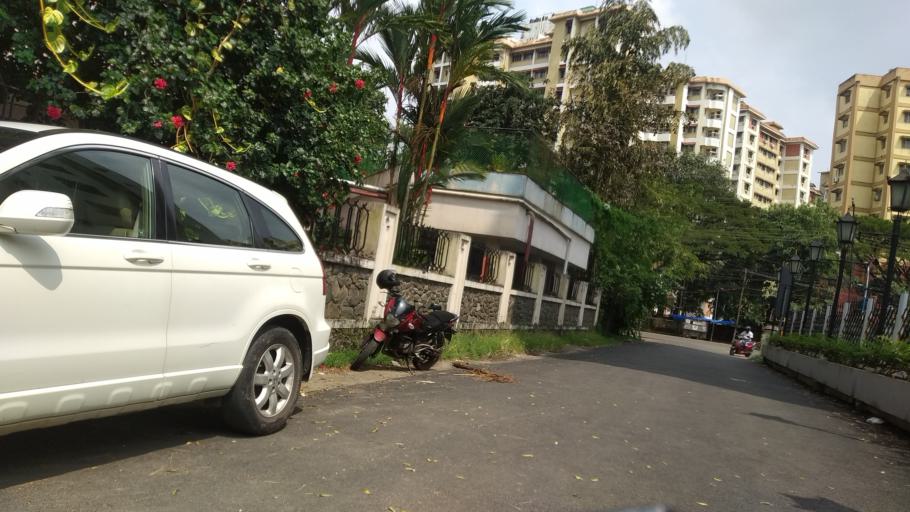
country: IN
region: Kerala
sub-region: Ernakulam
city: Cochin
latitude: 9.9541
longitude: 76.2961
